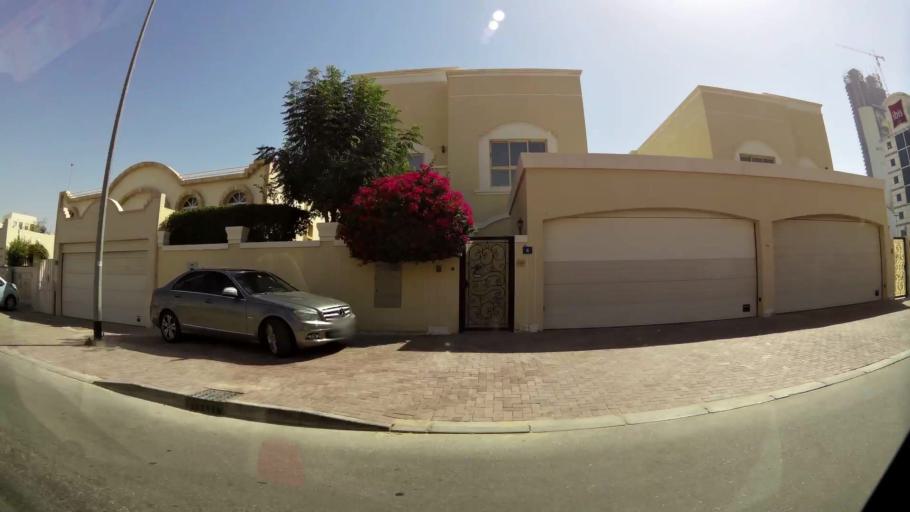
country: AE
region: Dubai
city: Dubai
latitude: 25.1078
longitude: 55.1844
